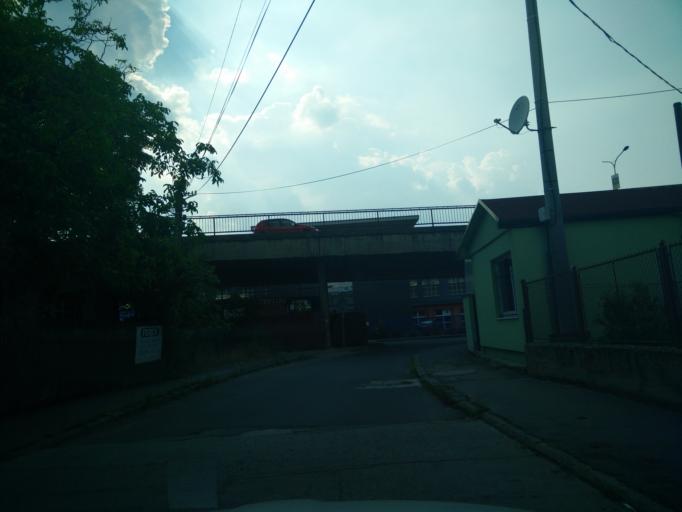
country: SK
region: Nitriansky
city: Prievidza
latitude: 48.7668
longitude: 18.6256
